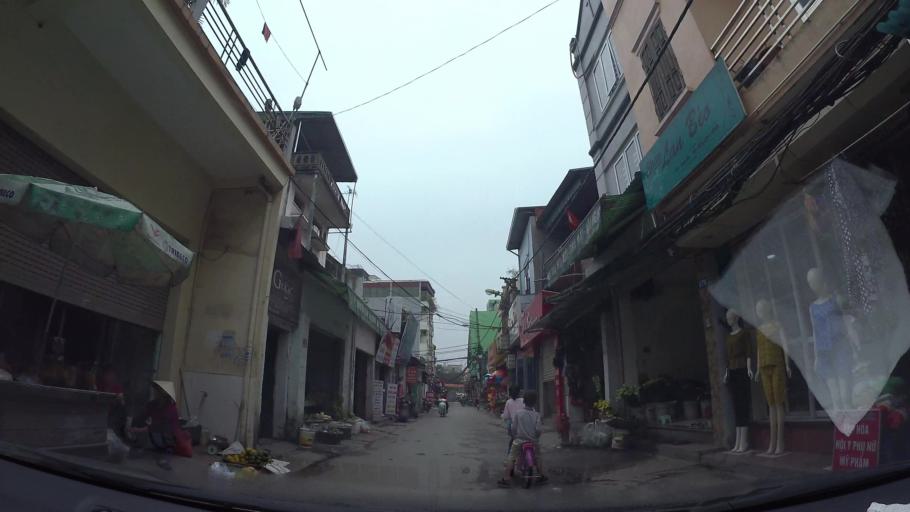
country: VN
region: Ha Noi
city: Hai BaTrung
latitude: 20.9835
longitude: 105.8871
